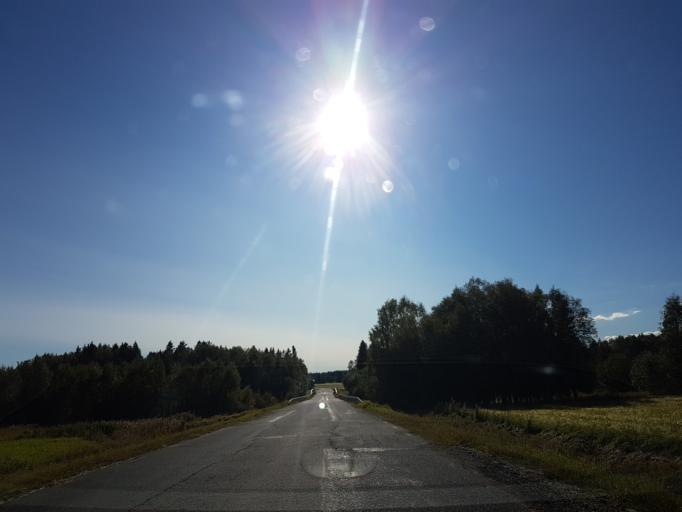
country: SE
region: Vaesterbotten
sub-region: Skelleftea Kommun
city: Burea
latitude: 64.3861
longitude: 21.3135
